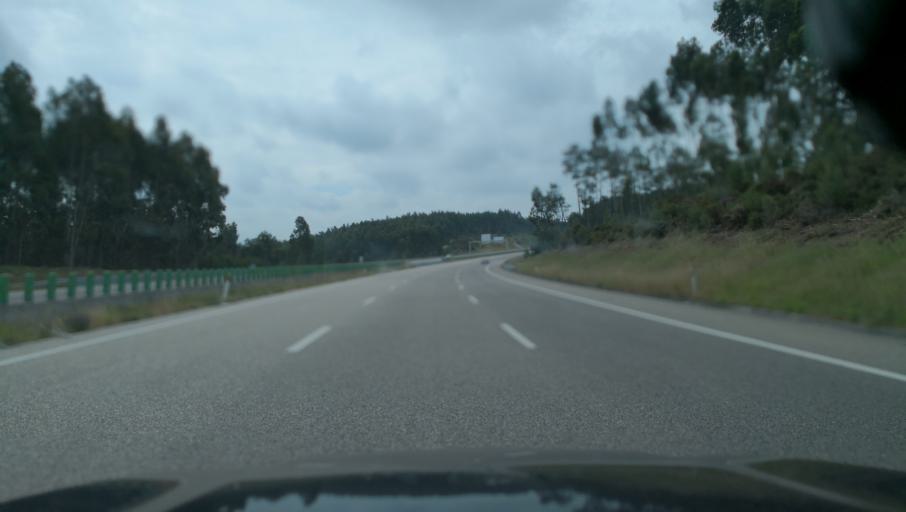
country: PT
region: Leiria
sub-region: Pombal
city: Lourical
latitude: 39.9825
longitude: -8.7863
